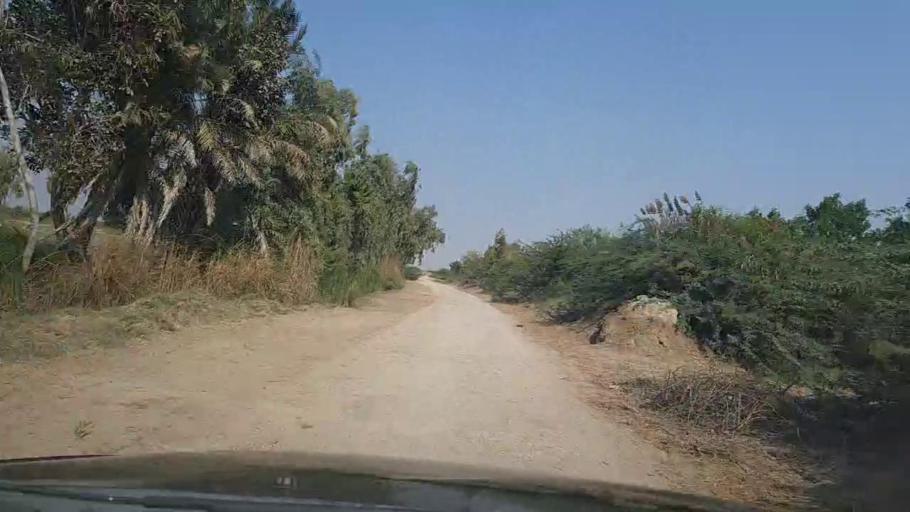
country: PK
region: Sindh
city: Thatta
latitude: 24.6332
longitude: 67.8135
